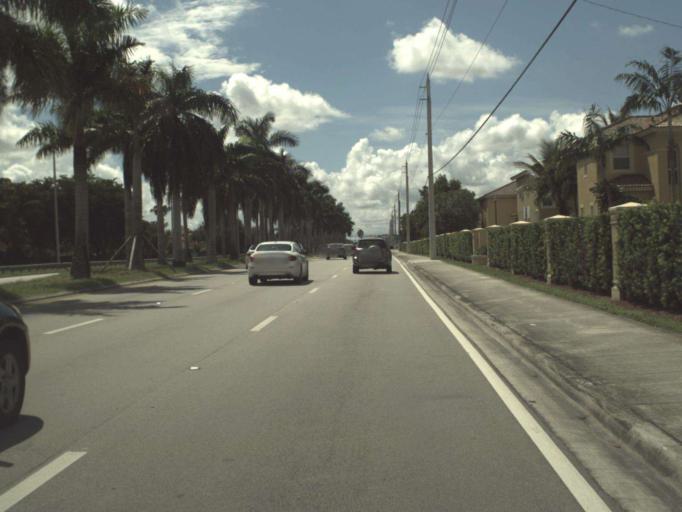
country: US
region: Florida
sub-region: Miami-Dade County
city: The Crossings
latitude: 25.6600
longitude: -80.4161
